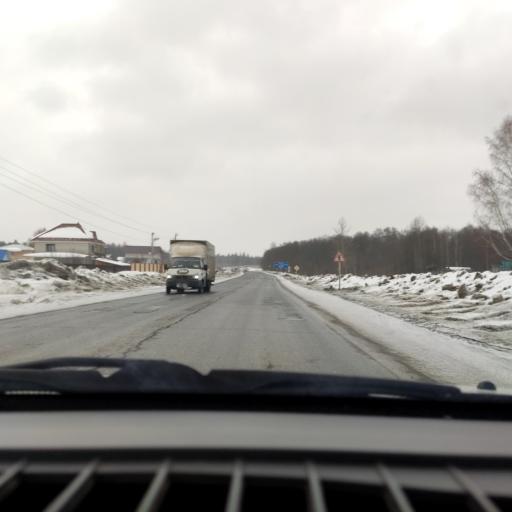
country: RU
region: Perm
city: Krasnokamsk
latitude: 58.0979
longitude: 55.8097
